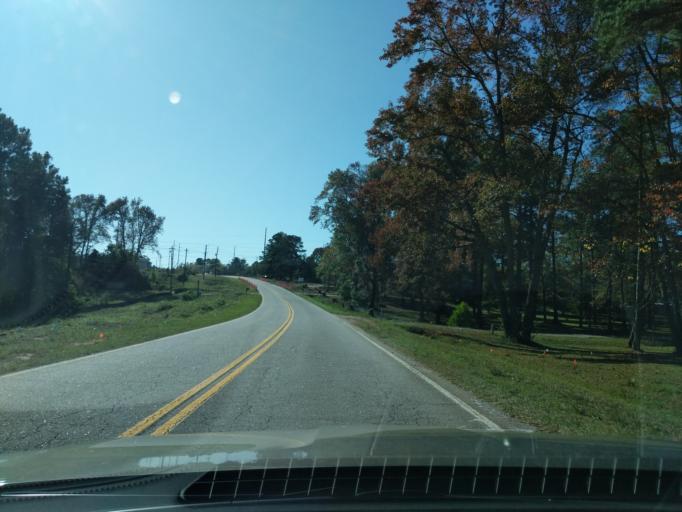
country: US
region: Georgia
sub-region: Columbia County
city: Grovetown
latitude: 33.4646
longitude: -82.1747
